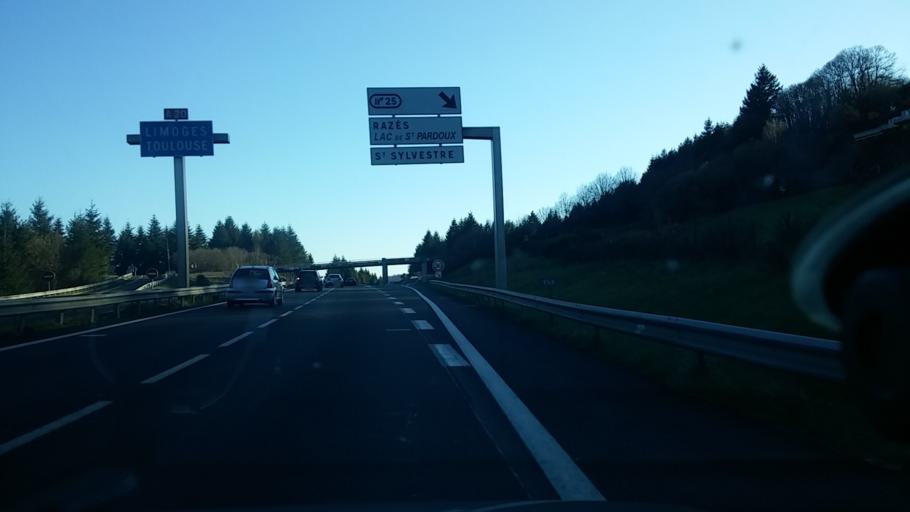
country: FR
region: Limousin
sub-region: Departement de la Haute-Vienne
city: Razes
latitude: 46.0276
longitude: 1.3461
